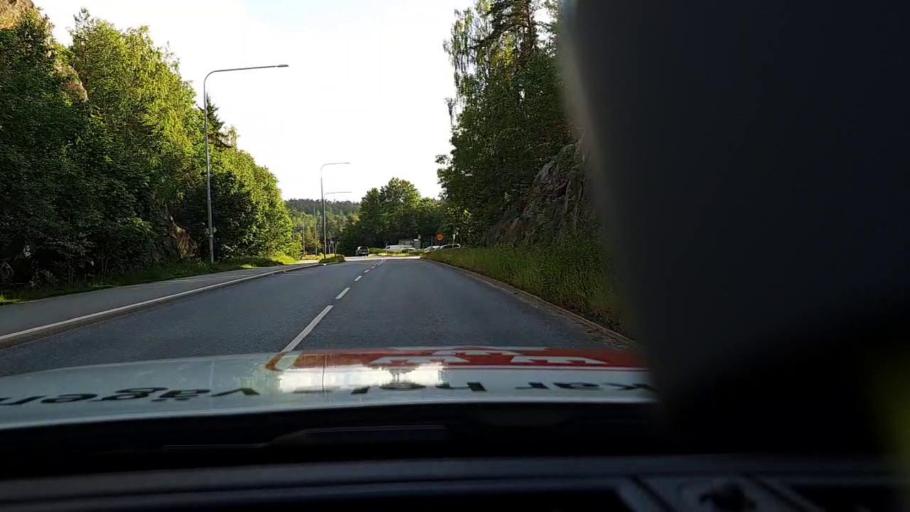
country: SE
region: Stockholm
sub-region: Huddinge Kommun
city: Huddinge
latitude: 59.2521
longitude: 17.9680
